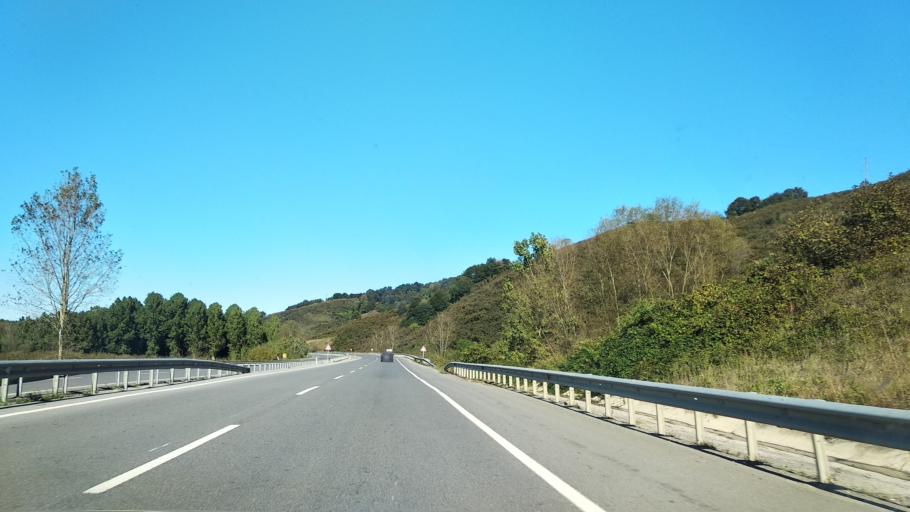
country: TR
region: Sakarya
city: Karasu
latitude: 41.0634
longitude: 30.6401
